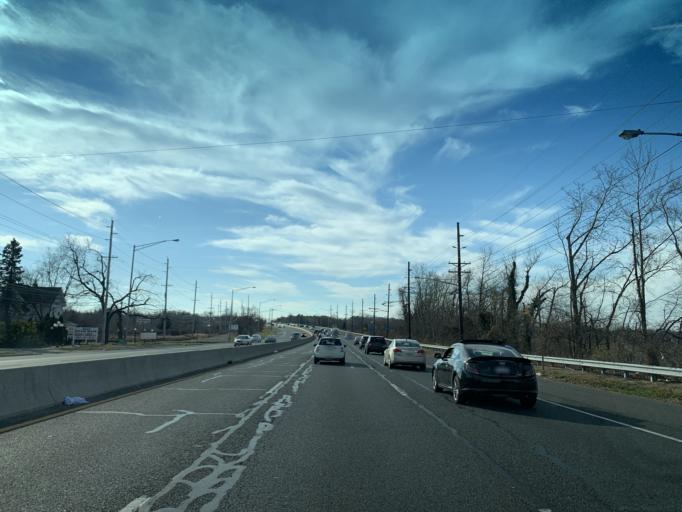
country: US
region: New Jersey
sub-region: Burlington County
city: Delanco
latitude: 40.0319
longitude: -74.9276
